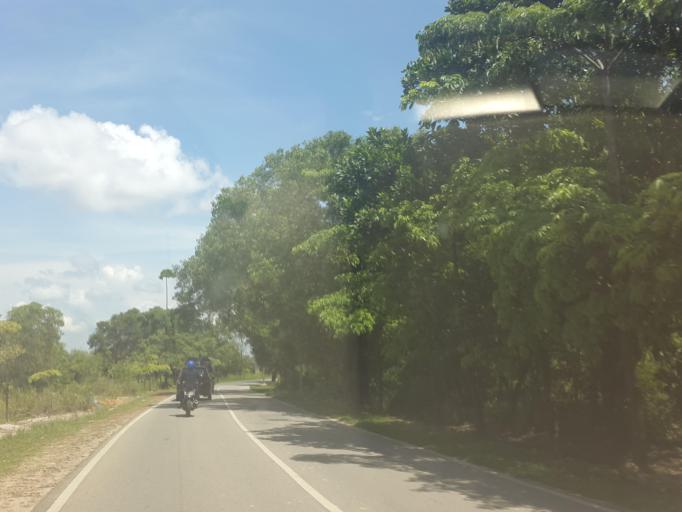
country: SG
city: Singapore
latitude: 1.0894
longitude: 103.9395
